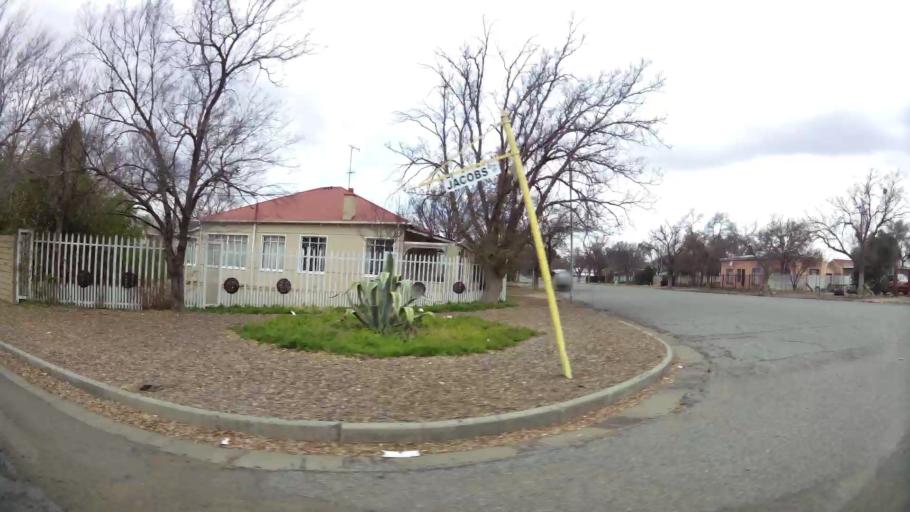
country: ZA
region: Orange Free State
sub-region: Fezile Dabi District Municipality
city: Kroonstad
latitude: -27.6540
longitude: 27.2433
